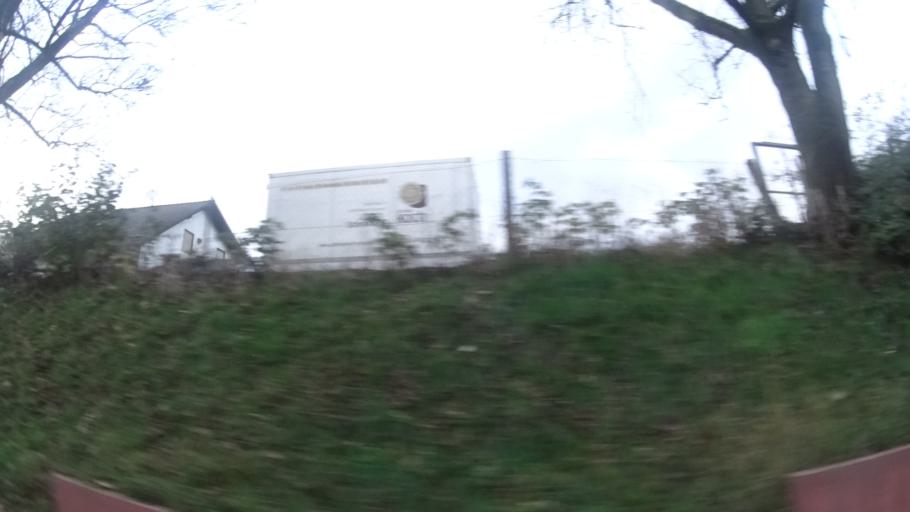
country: DE
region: Hesse
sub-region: Regierungsbezirk Kassel
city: Hosenfeld
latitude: 50.4617
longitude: 9.4798
